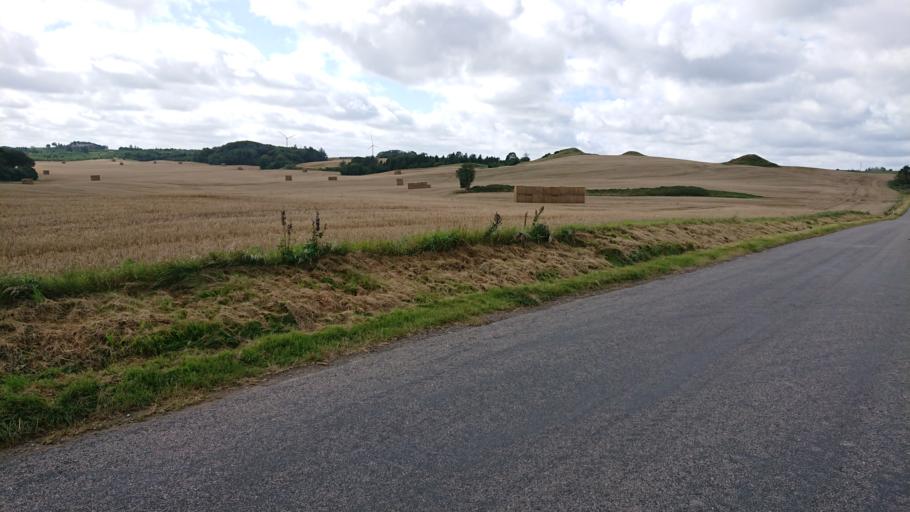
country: DK
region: North Denmark
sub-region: Hjorring Kommune
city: Sindal
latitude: 57.4362
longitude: 10.3283
